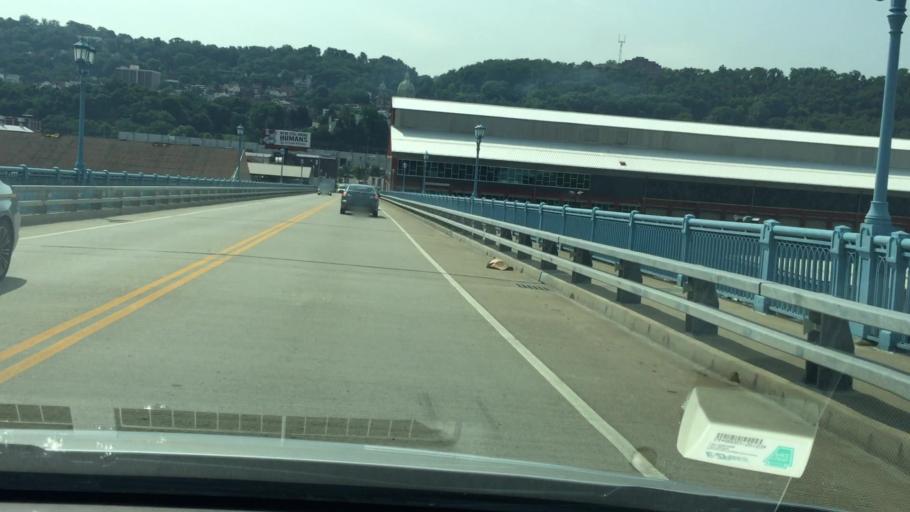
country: US
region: Pennsylvania
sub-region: Allegheny County
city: Millvale
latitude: 40.4622
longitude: -79.9742
